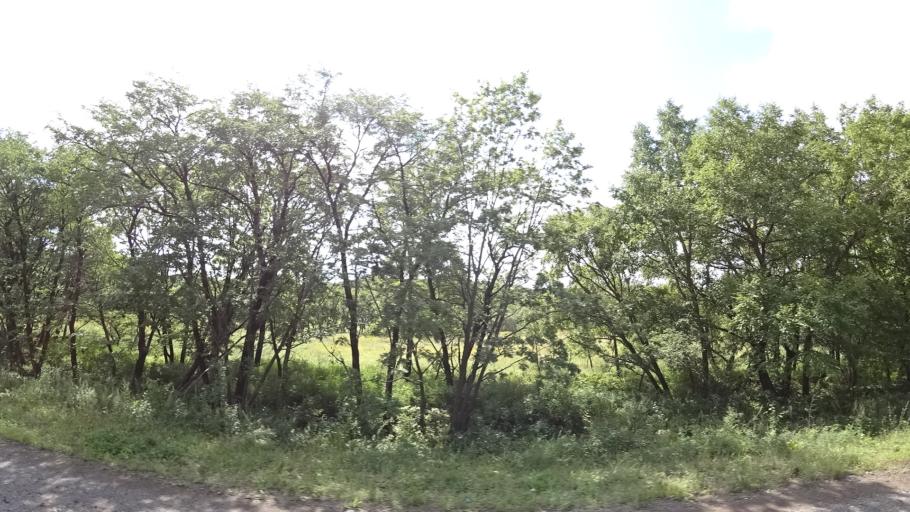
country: RU
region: Primorskiy
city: Lyalichi
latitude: 44.1496
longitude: 132.3935
